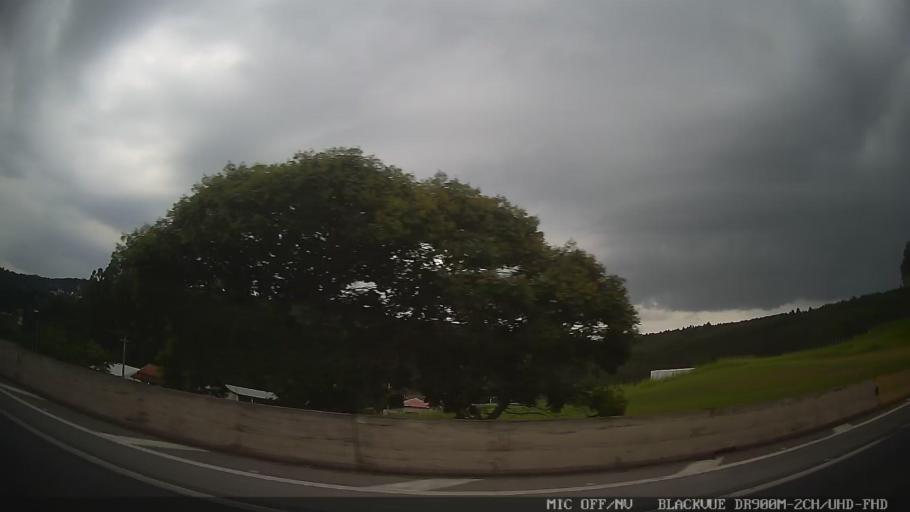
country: BR
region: Sao Paulo
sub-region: Jarinu
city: Jarinu
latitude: -23.0312
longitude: -46.7261
